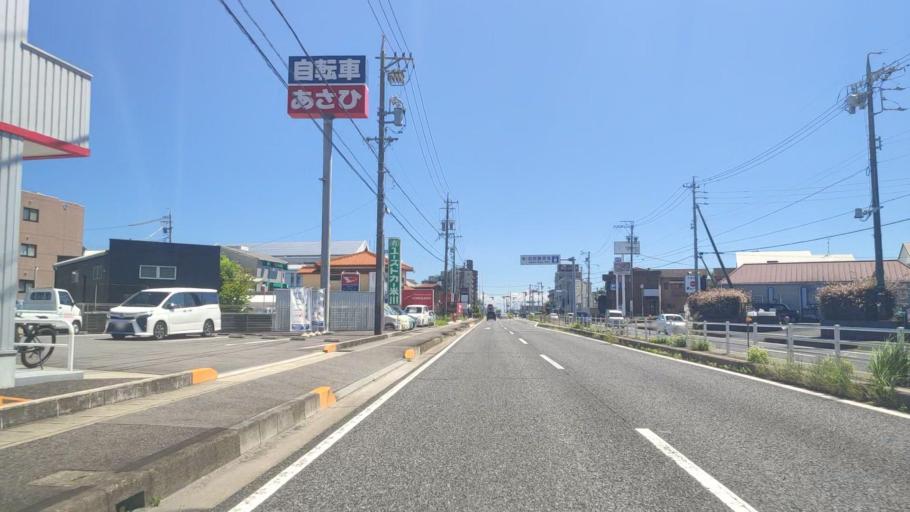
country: JP
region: Mie
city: Suzuka
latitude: 34.8493
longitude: 136.5897
